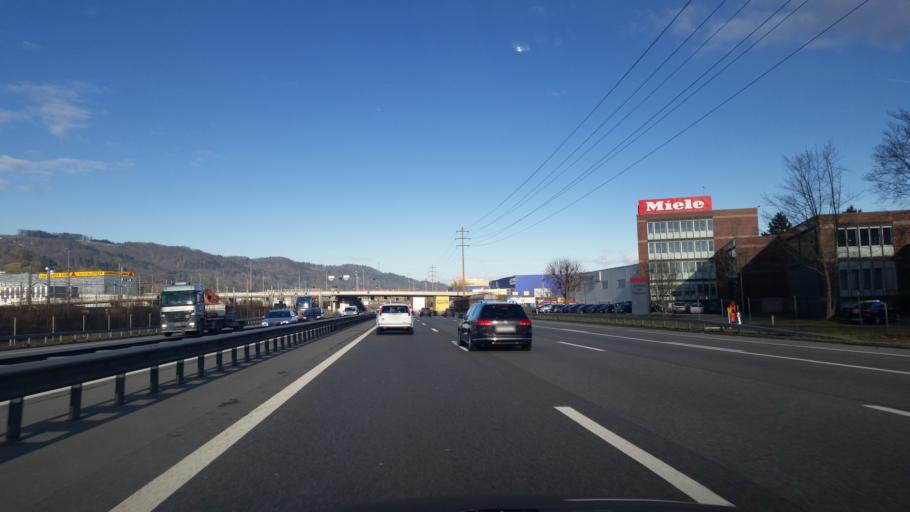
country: CH
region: Aargau
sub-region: Bezirk Baden
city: Spreitenbach
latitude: 47.4272
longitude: 8.3730
